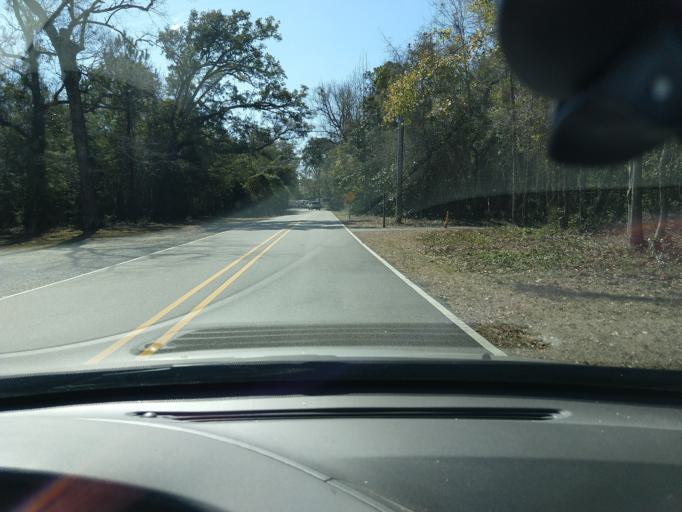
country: US
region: Mississippi
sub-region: Jackson County
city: Gulf Park Estates
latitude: 30.3991
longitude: -88.7950
